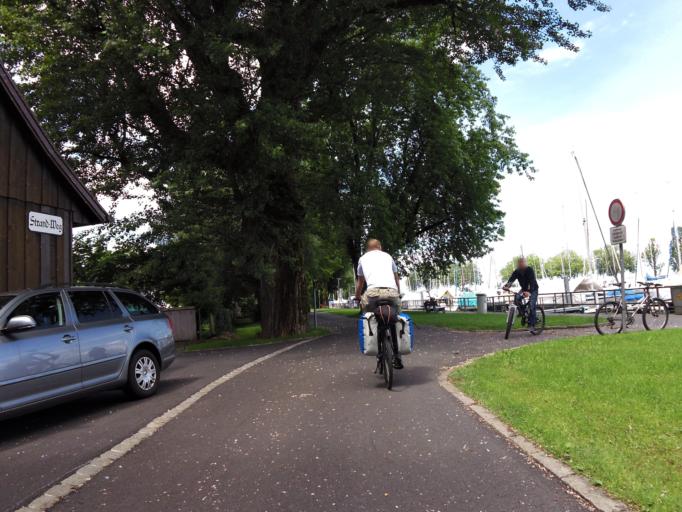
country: AT
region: Vorarlberg
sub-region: Politischer Bezirk Bregenz
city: Bregenz
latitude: 47.5058
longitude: 9.7276
